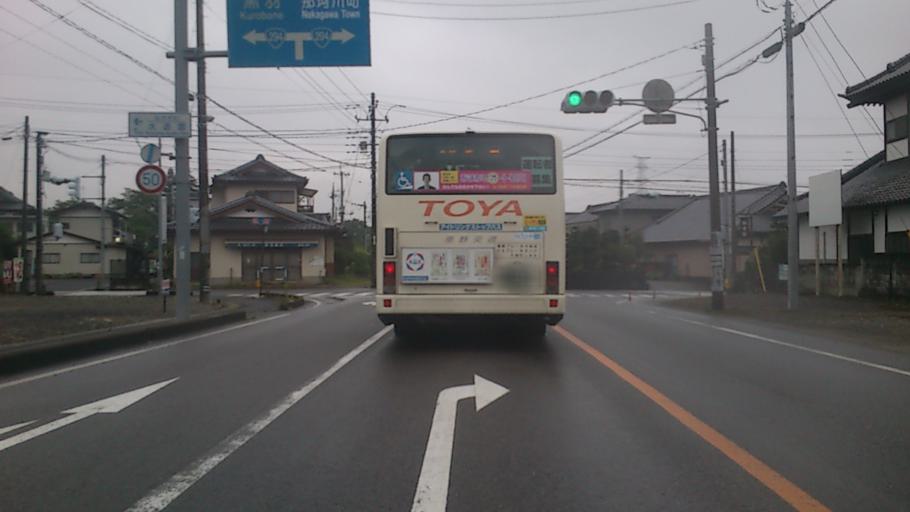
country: JP
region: Tochigi
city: Otawara
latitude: 36.7907
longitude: 140.1213
